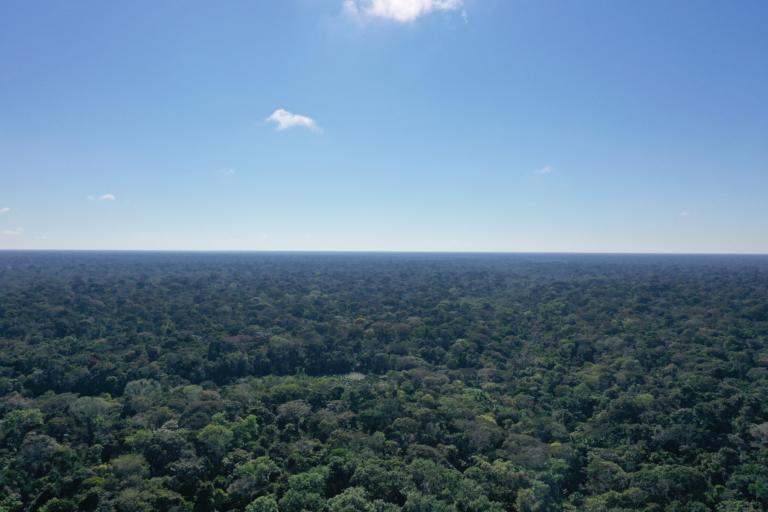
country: PE
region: Madre de Dios
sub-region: Provincia de Tambopata
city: Puerto Maldonado
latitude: -12.1990
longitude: -68.6326
